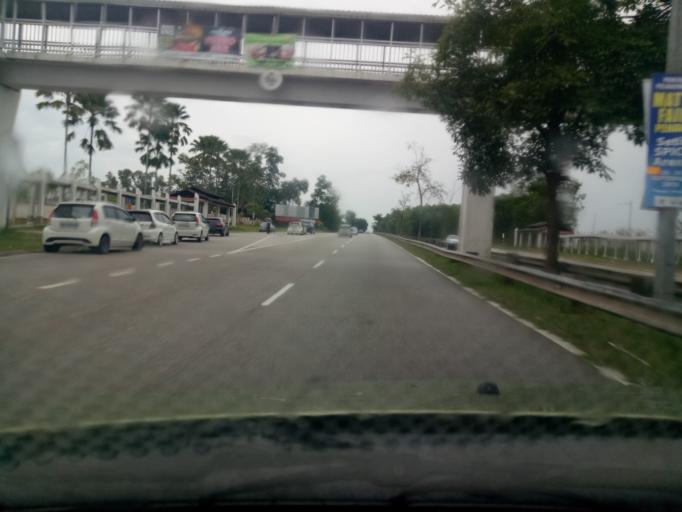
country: MY
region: Kedah
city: Sungai Petani
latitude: 5.6681
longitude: 100.5172
